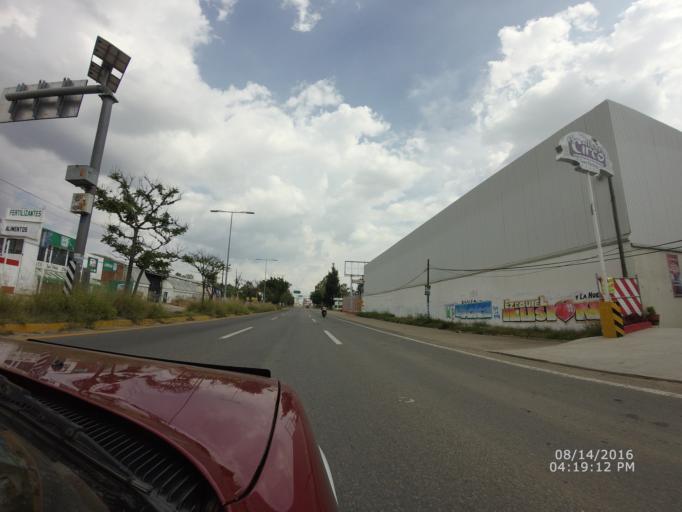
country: MX
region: Oaxaca
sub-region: San Lorenzo Cacaotepec
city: Santiago Etla
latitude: 17.1386
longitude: -96.7760
